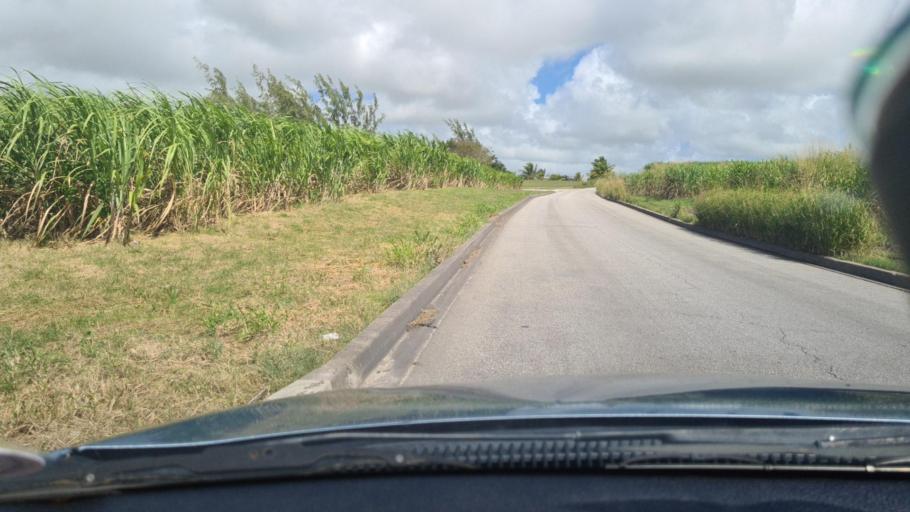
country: BB
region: Christ Church
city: Oistins
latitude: 13.0853
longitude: -59.5295
